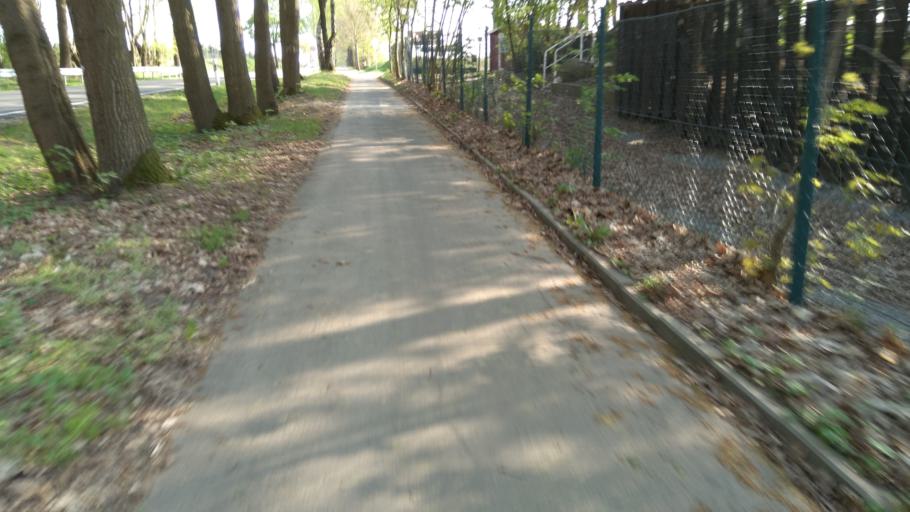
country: DE
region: Lower Saxony
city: Buxtehude
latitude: 53.4470
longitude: 9.6937
